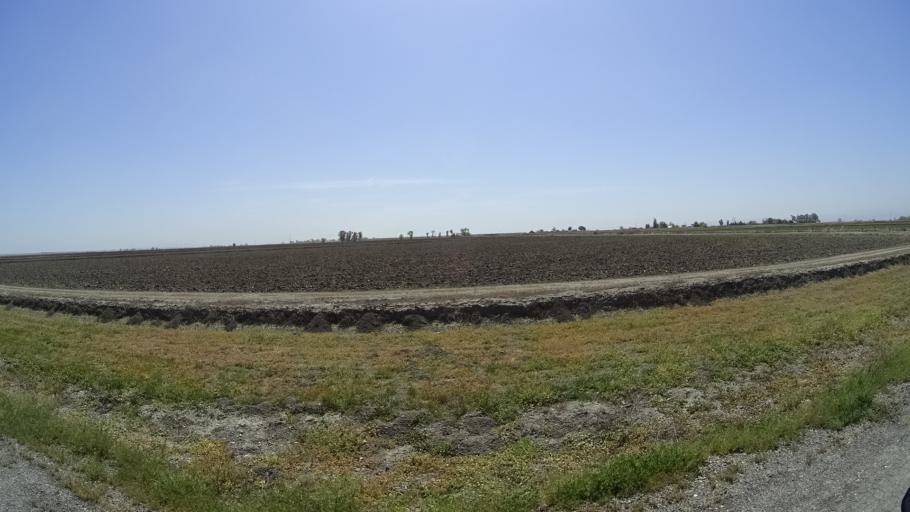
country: US
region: California
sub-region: Glenn County
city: Willows
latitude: 39.5311
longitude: -122.1067
